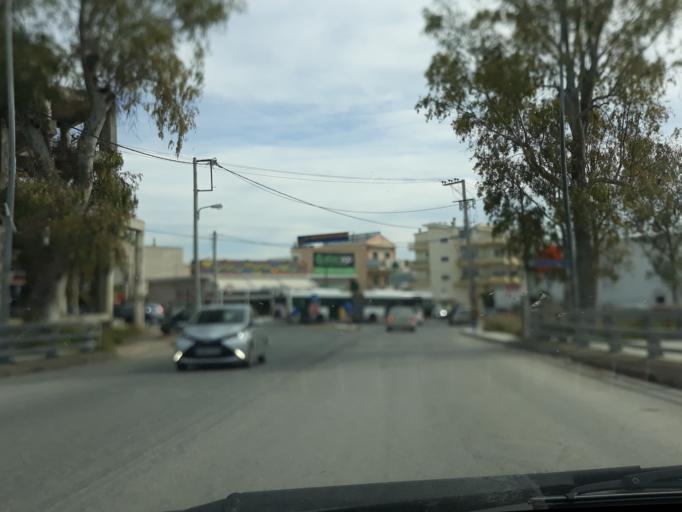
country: GR
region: Attica
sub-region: Nomarchia Anatolikis Attikis
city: Acharnes
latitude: 38.0968
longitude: 23.7384
